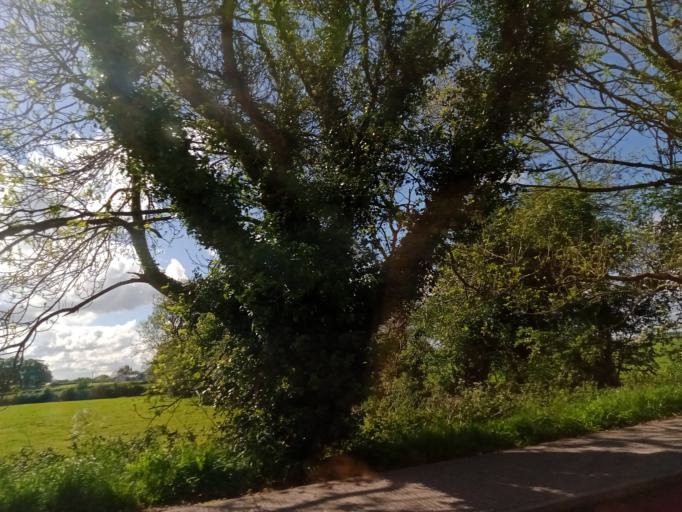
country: IE
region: Munster
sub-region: County Cork
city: Fermoy
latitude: 52.1547
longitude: -8.2781
